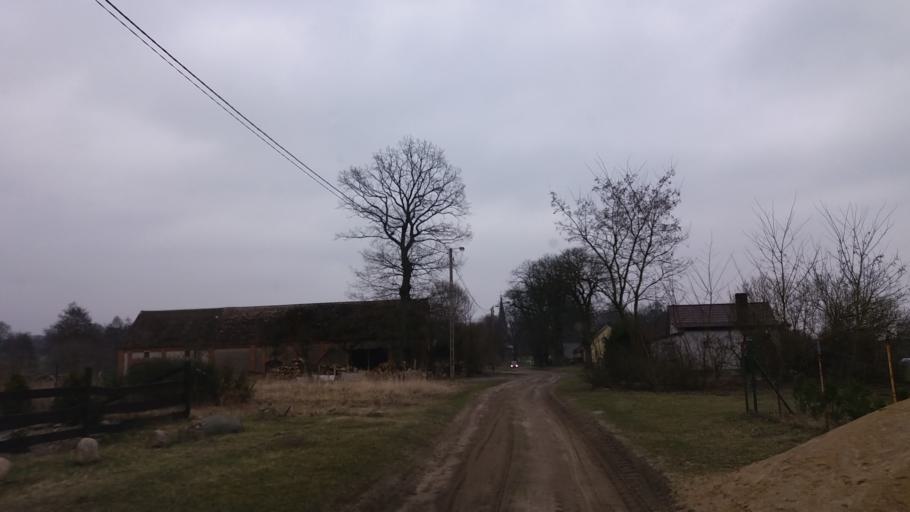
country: PL
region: West Pomeranian Voivodeship
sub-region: Powiat choszczenski
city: Recz
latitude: 53.1921
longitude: 15.5027
